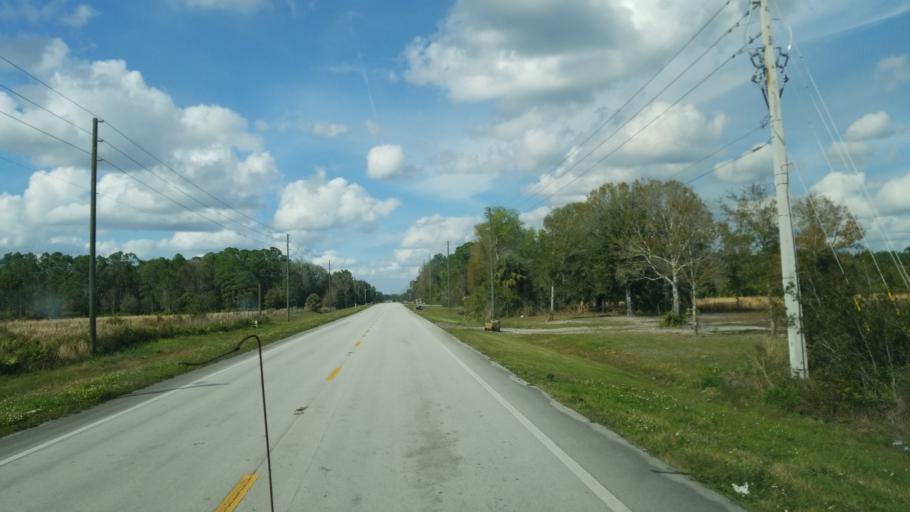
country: US
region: Florida
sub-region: Osceola County
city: Saint Cloud
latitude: 28.0781
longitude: -81.0699
